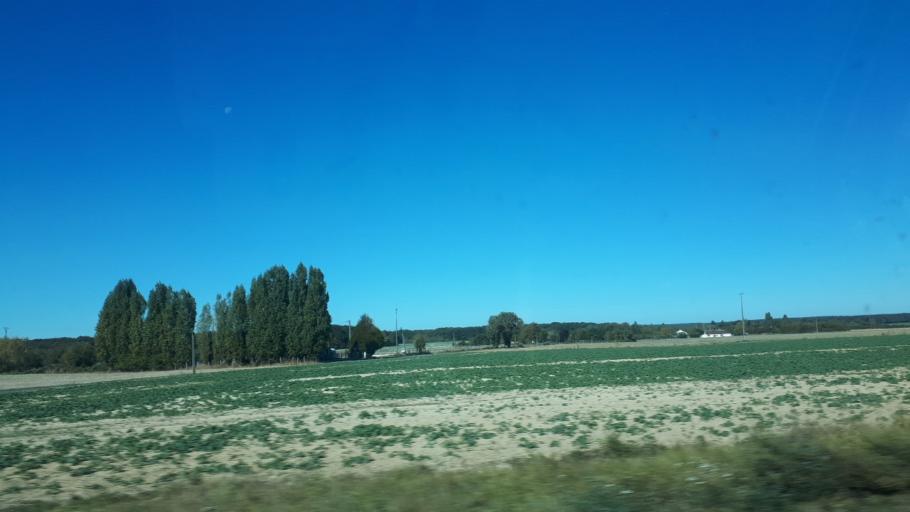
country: FR
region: Centre
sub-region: Departement du Loir-et-Cher
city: Moree
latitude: 47.9174
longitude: 1.1917
